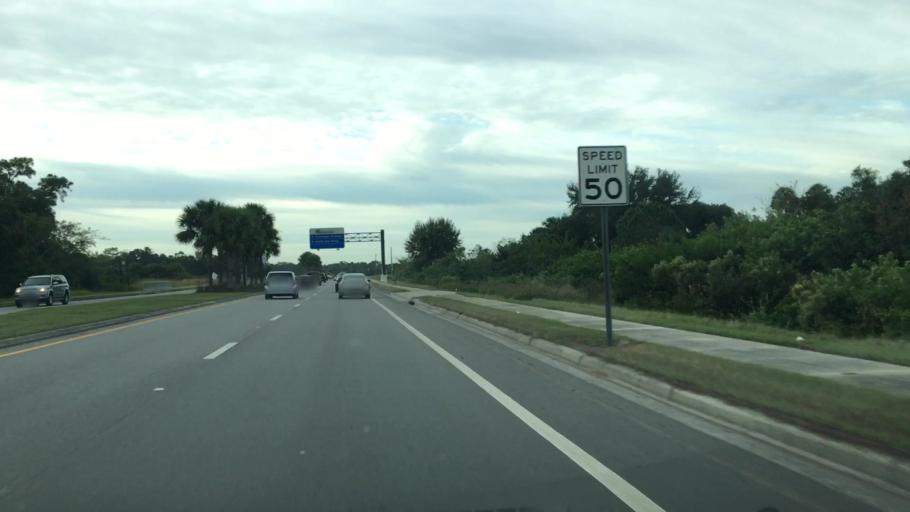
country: US
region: Florida
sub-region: Seminole County
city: Midway
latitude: 28.7799
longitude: -81.2105
